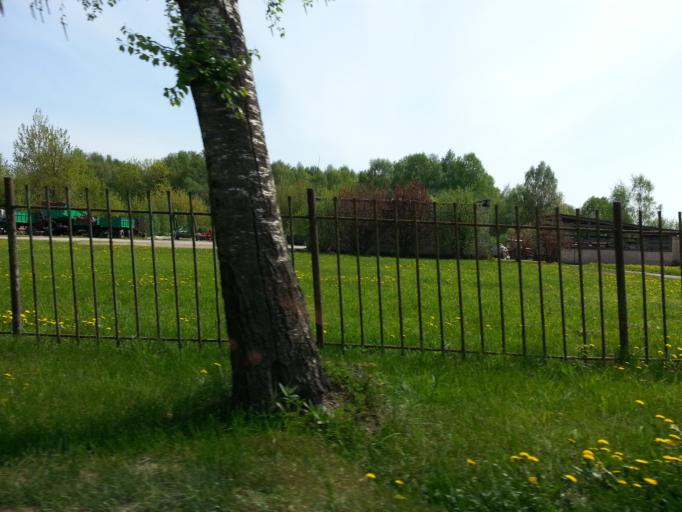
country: LT
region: Panevezys
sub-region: Panevezys City
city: Panevezys
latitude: 55.8977
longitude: 24.2374
